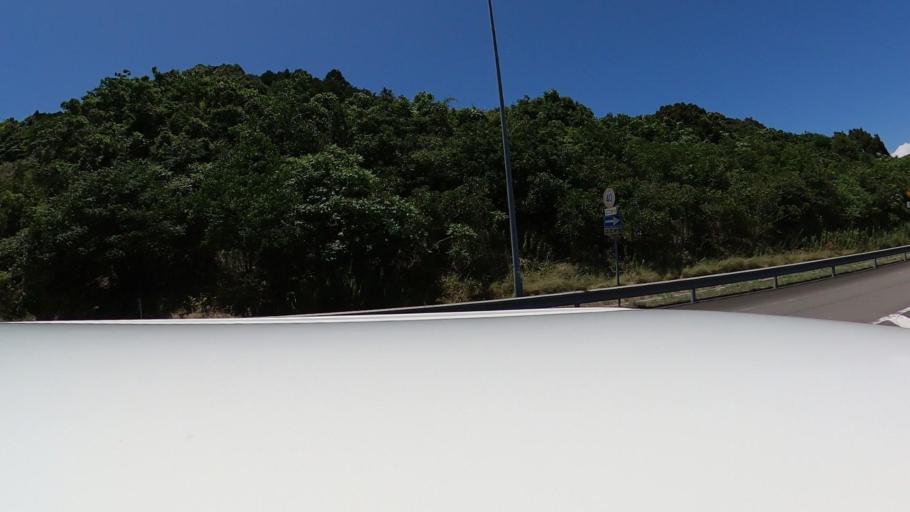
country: JP
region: Miyazaki
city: Nobeoka
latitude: 32.5259
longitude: 131.6653
